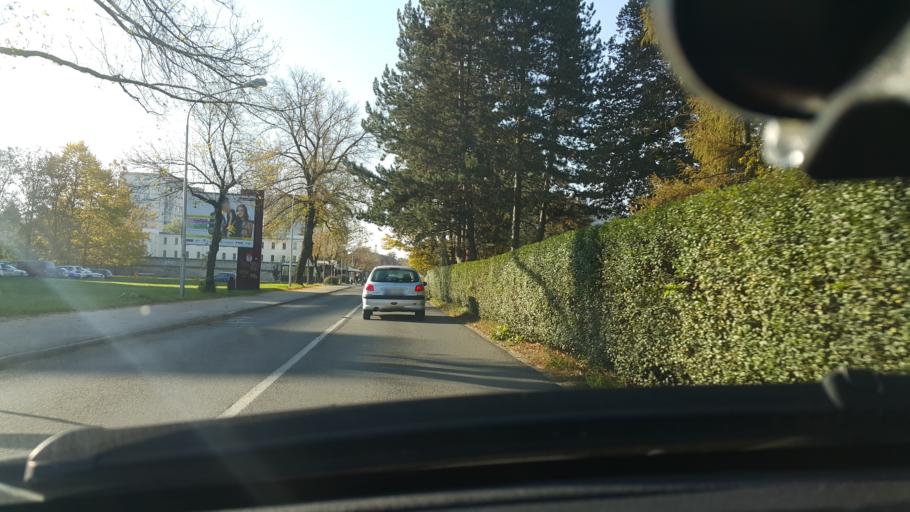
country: SI
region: Maribor
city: Maribor
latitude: 46.5511
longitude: 15.6461
